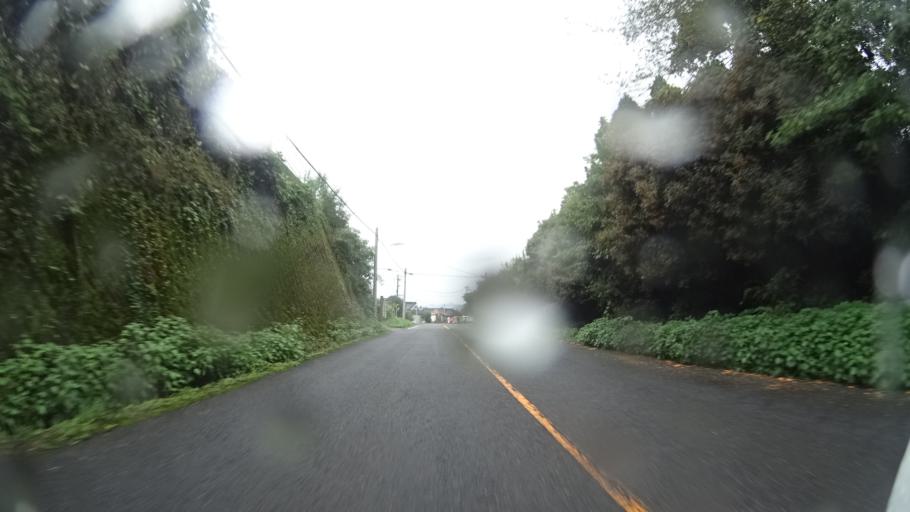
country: JP
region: Kagoshima
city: Kajiki
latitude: 31.7922
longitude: 130.6741
